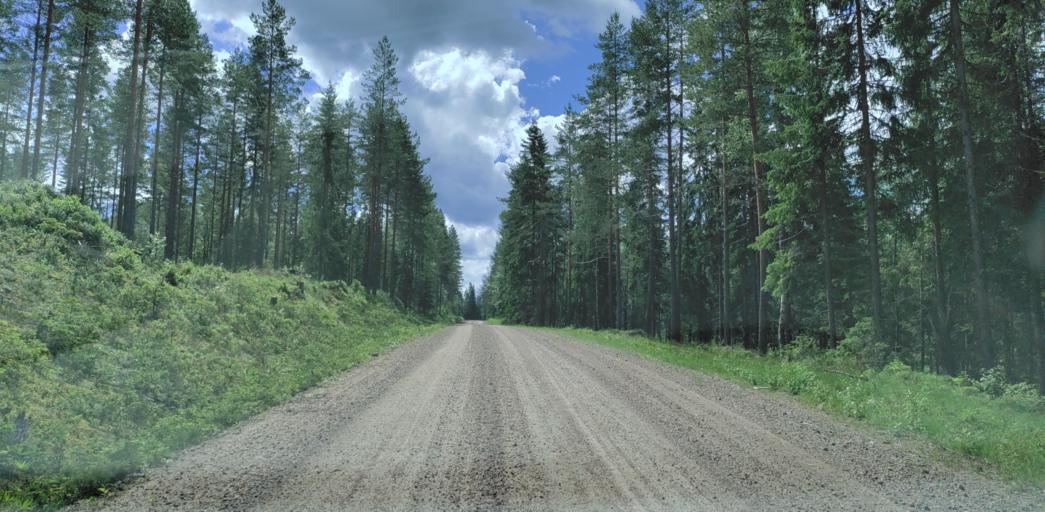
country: SE
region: Vaermland
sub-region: Hagfors Kommun
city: Ekshaerad
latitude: 60.0990
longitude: 13.3496
